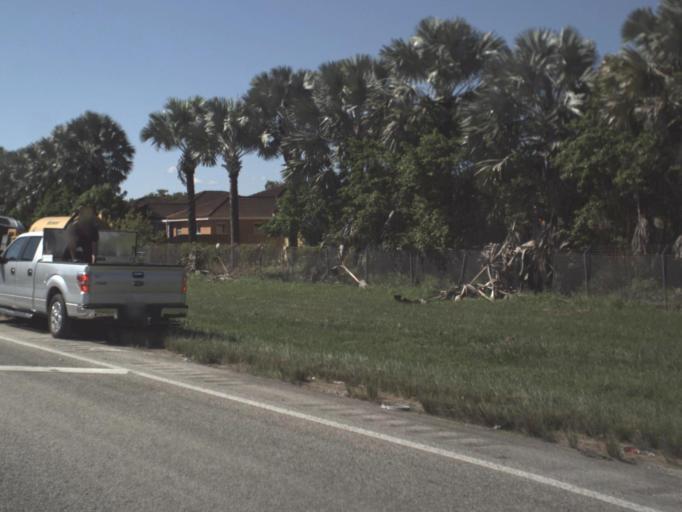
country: US
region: Florida
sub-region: Miami-Dade County
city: Goulds
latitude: 25.5430
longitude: -80.3633
